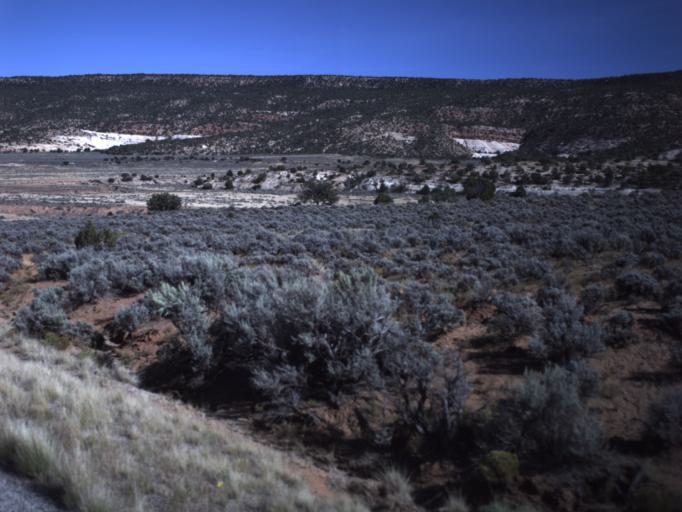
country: US
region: Utah
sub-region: San Juan County
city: Monticello
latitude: 38.0067
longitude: -109.4451
